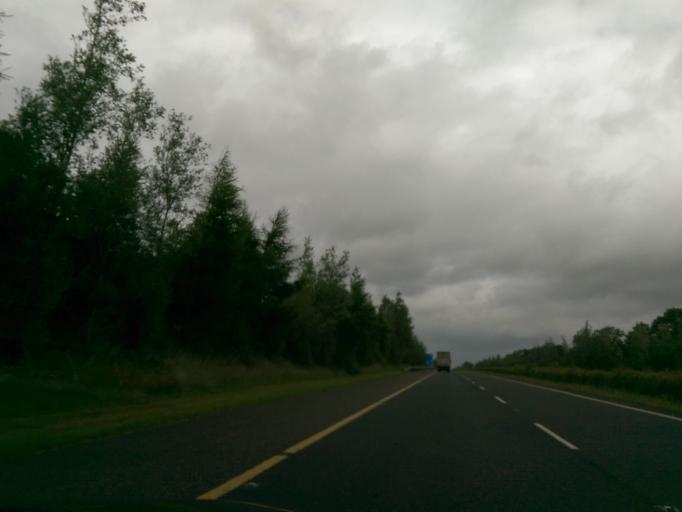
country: IE
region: Munster
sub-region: An Clar
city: Newmarket on Fergus
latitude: 52.7394
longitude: -8.8923
